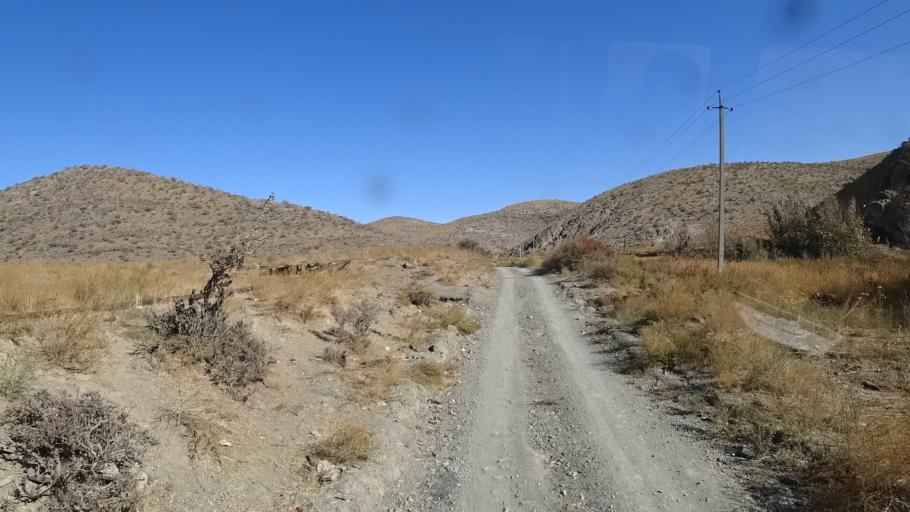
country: UZ
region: Navoiy
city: Nurota
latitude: 40.3106
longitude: 65.6228
